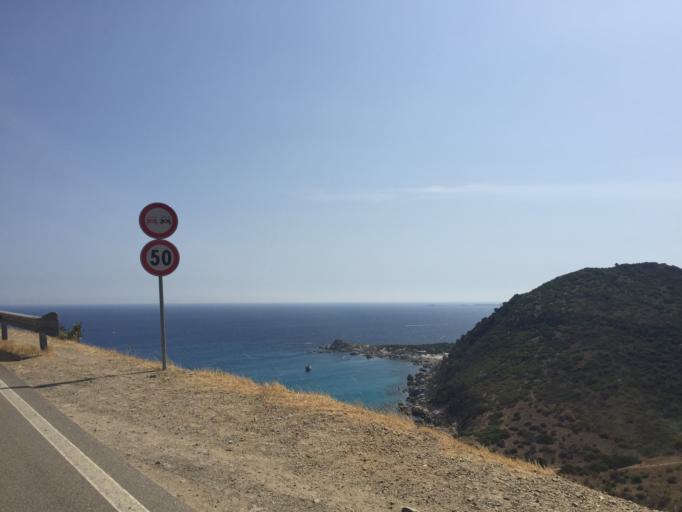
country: IT
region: Sardinia
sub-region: Provincia di Cagliari
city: Villasimius
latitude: 39.1402
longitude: 9.5589
